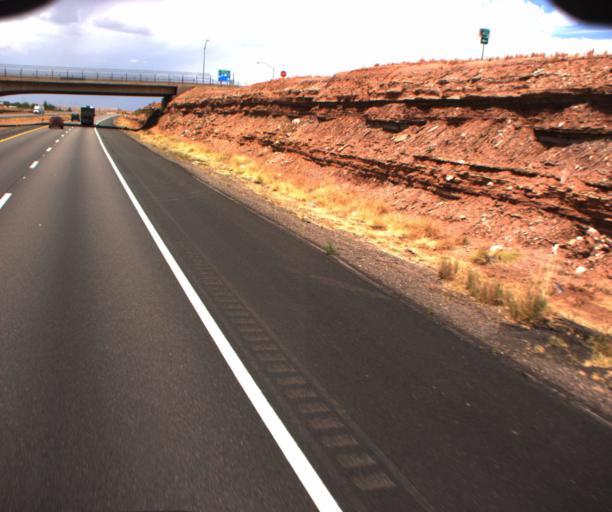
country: US
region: Arizona
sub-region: Navajo County
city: Winslow
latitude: 35.0380
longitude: -110.7229
